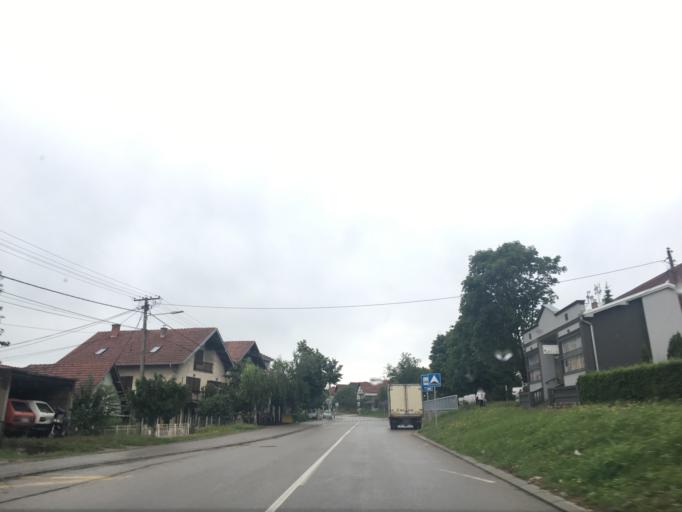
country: RS
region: Central Serbia
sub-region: Nisavski Okrug
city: Aleksinac
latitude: 43.5422
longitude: 21.7015
